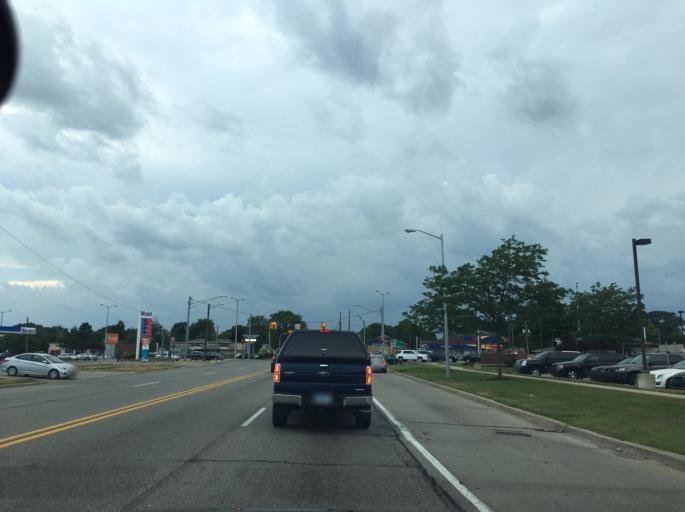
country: US
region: Michigan
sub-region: Macomb County
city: Roseville
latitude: 42.5099
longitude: -82.9270
